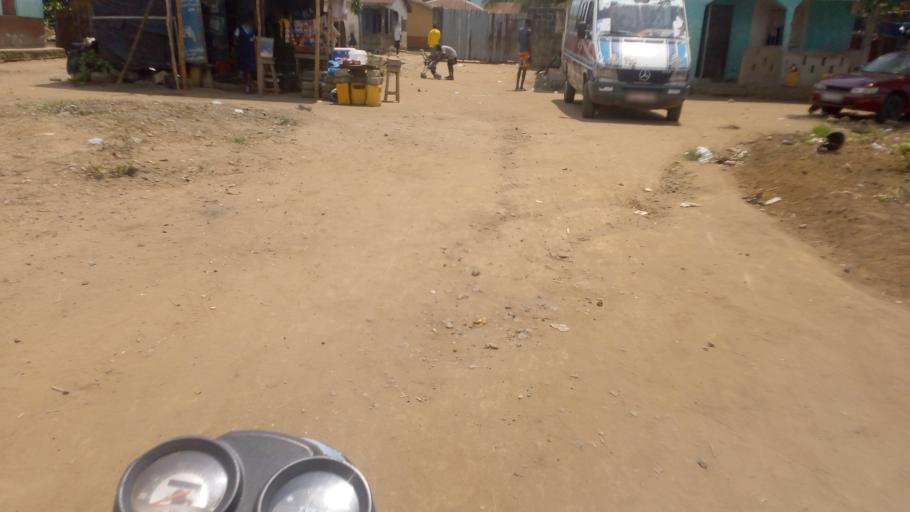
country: SL
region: Western Area
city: Waterloo
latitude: 8.3239
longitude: -13.0745
